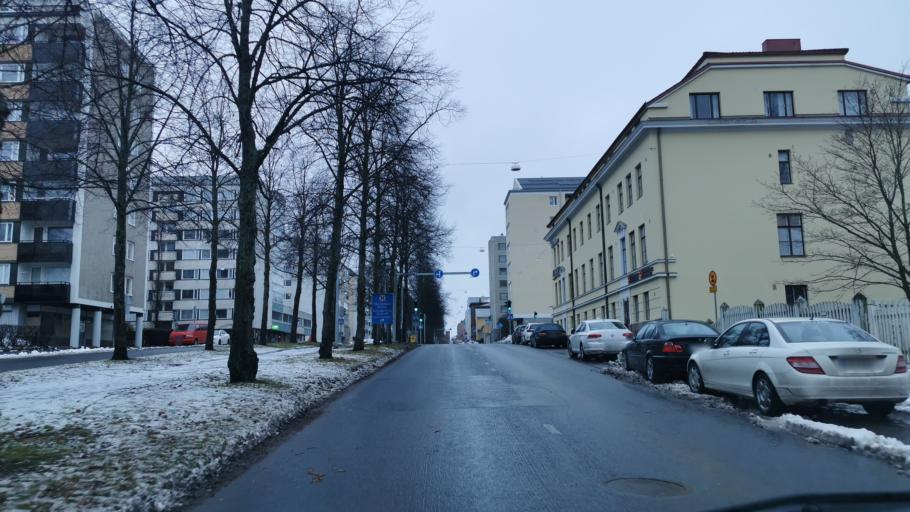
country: FI
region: Ostrobothnia
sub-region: Vaasa
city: Vaasa
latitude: 63.1005
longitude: 21.6050
